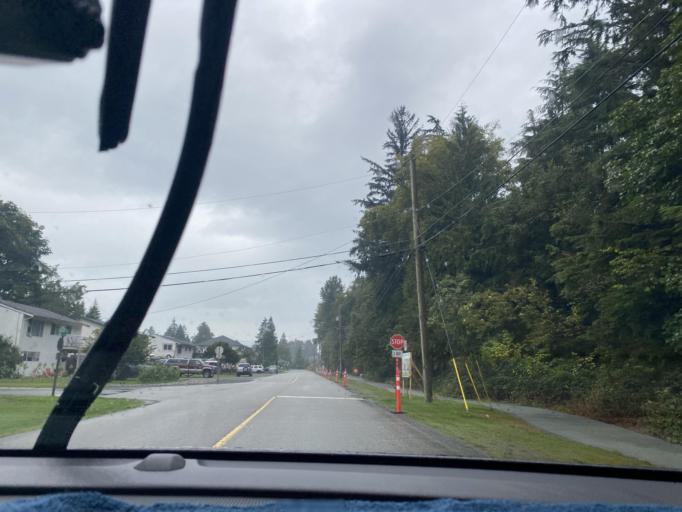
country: CA
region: British Columbia
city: Agassiz
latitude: 49.2938
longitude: -121.7775
